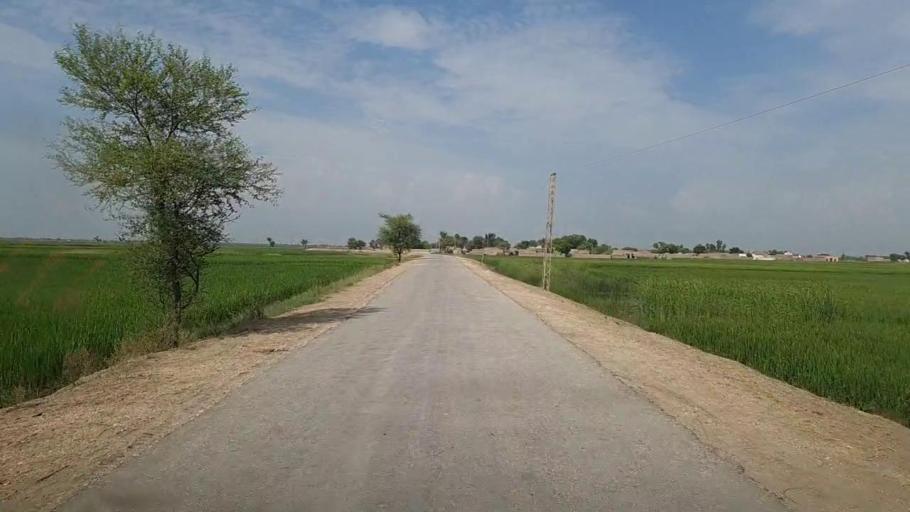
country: PK
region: Sindh
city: Thul
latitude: 28.2645
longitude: 68.8172
